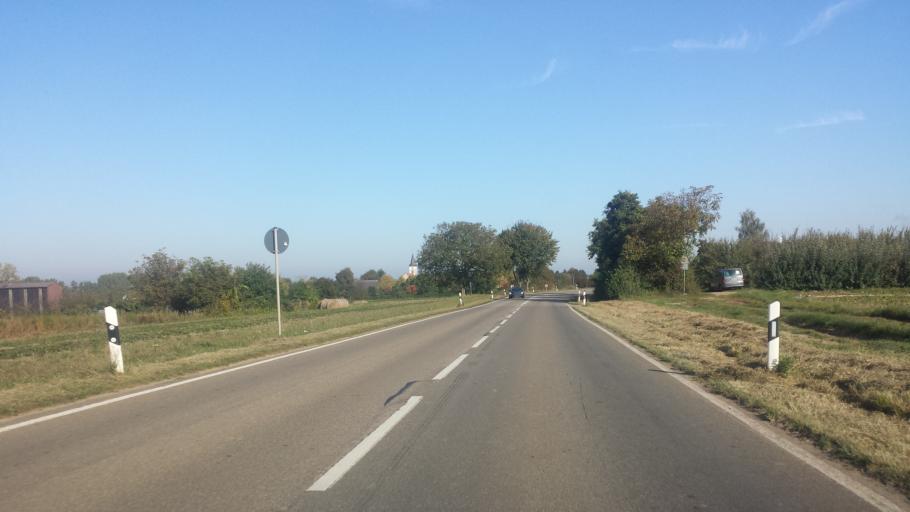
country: DE
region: Rheinland-Pfalz
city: Schwegenheim
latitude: 49.2650
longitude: 8.3143
